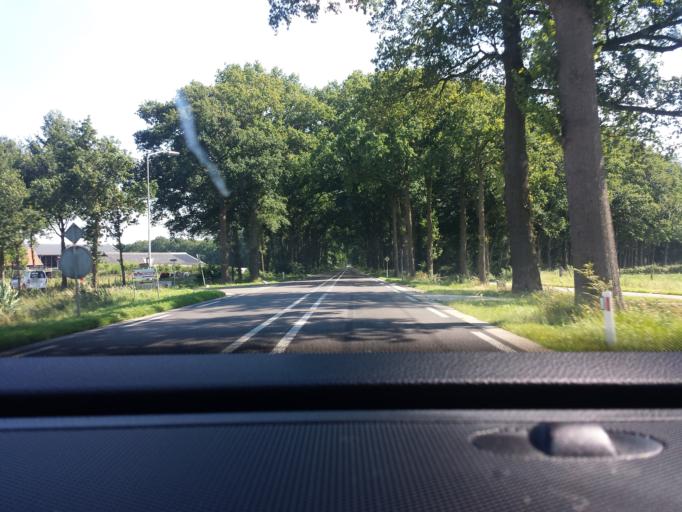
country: NL
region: Gelderland
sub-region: Gemeente Bronckhorst
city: Baak
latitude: 52.0276
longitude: 6.2165
